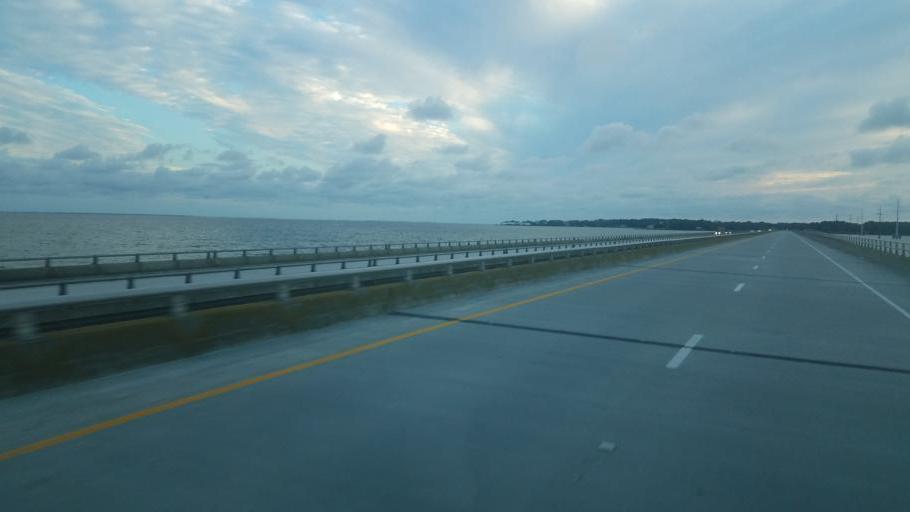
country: US
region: North Carolina
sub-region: Dare County
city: Southern Shores
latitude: 36.0849
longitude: -75.7749
